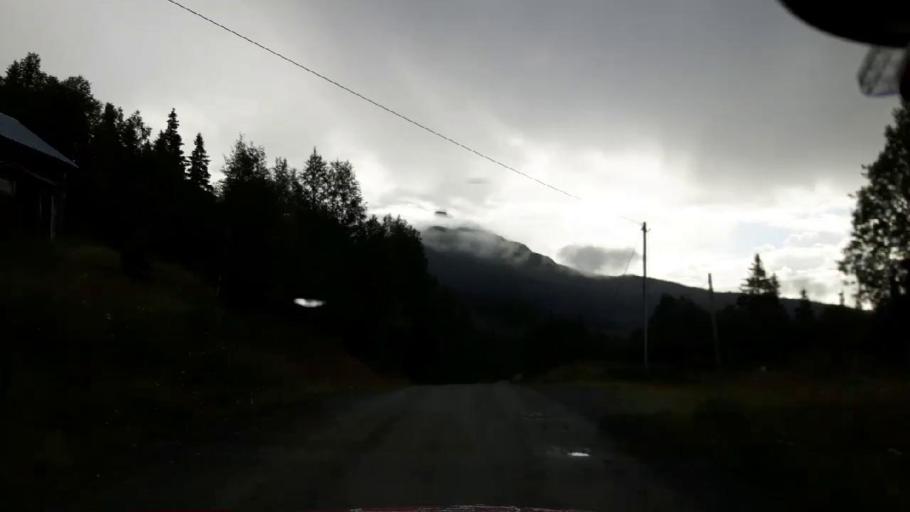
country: NO
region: Nordland
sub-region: Hattfjelldal
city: Hattfjelldal
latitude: 64.8846
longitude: 14.8294
